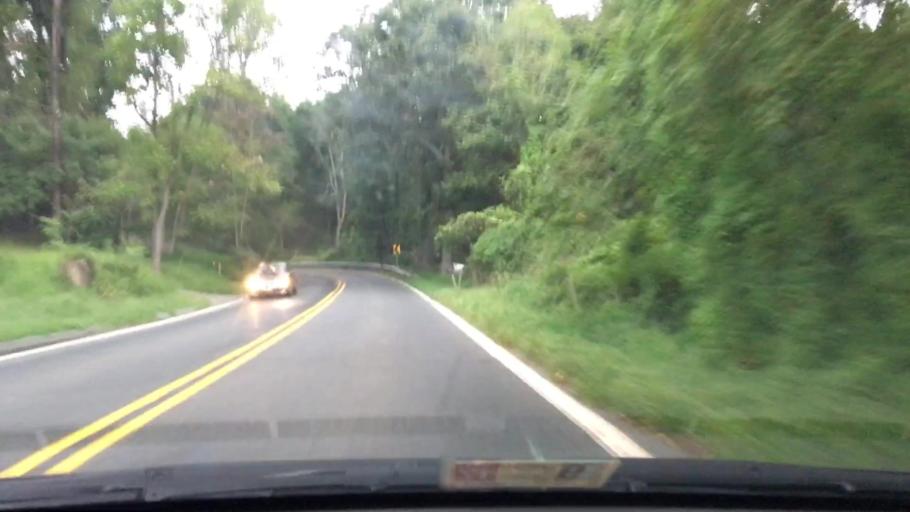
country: US
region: Maryland
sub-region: Montgomery County
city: Montgomery Village
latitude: 39.2059
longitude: -77.1678
